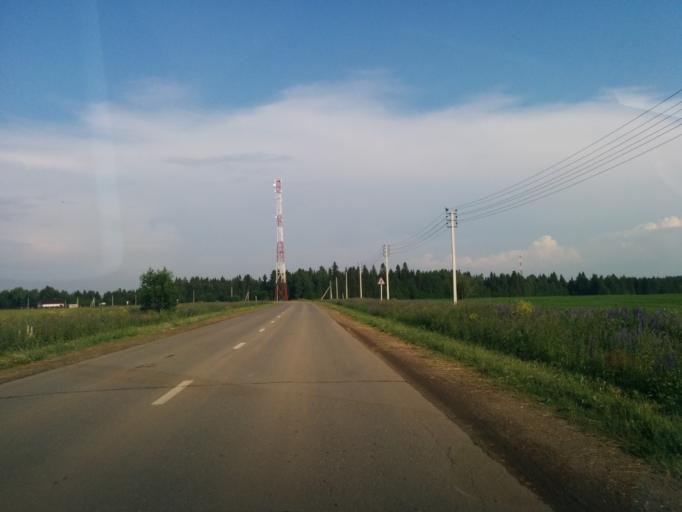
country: RU
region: Perm
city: Polazna
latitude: 58.2386
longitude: 56.2747
